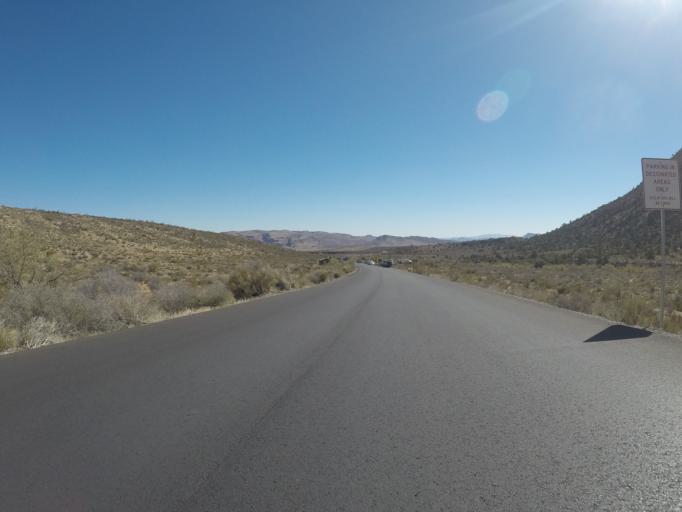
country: US
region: Nevada
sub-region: Clark County
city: Summerlin South
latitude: 36.1513
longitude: -115.4853
